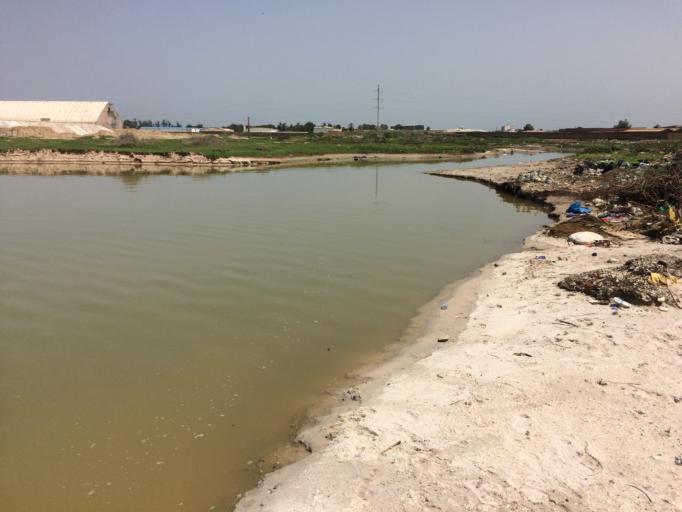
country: SN
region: Dakar
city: Pikine
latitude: 14.7345
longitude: -17.3390
